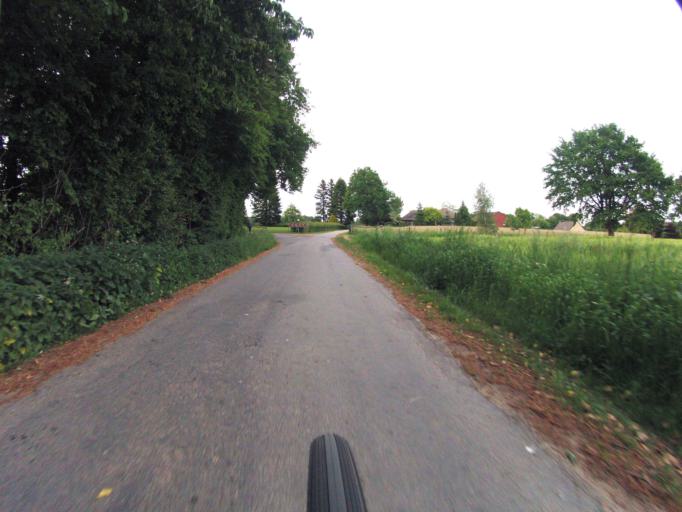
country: DE
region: North Rhine-Westphalia
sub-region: Regierungsbezirk Munster
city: Tecklenburg
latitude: 52.2664
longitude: 7.8058
